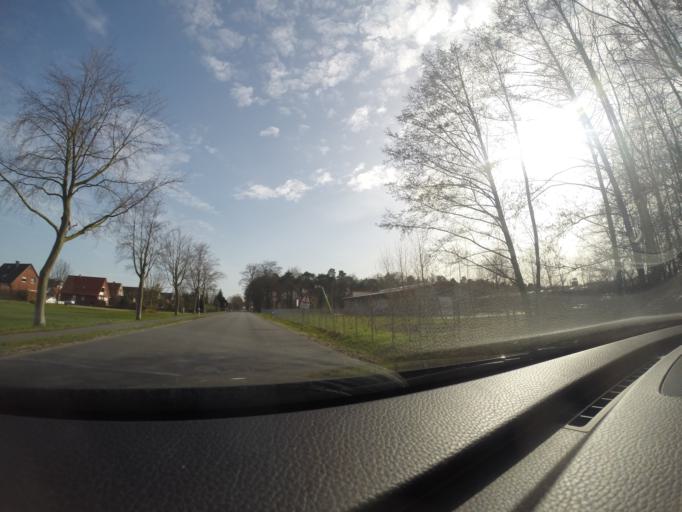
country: DE
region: North Rhine-Westphalia
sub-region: Regierungsbezirk Munster
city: Legden
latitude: 52.0382
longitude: 7.0914
